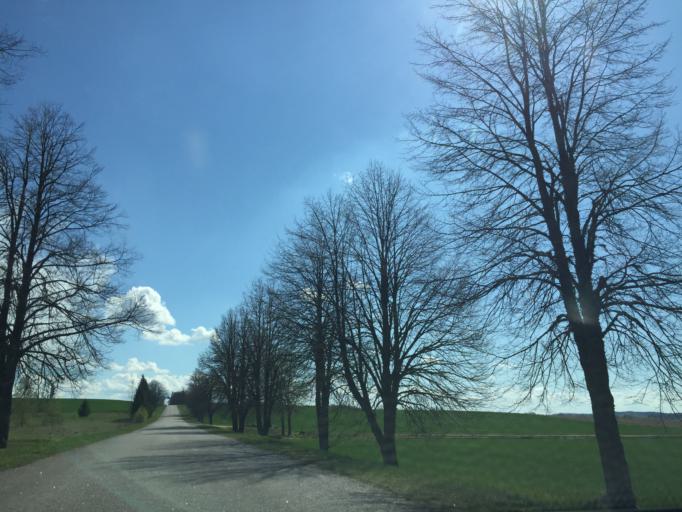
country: LV
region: Strenci
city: Strenci
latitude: 57.5549
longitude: 25.7123
